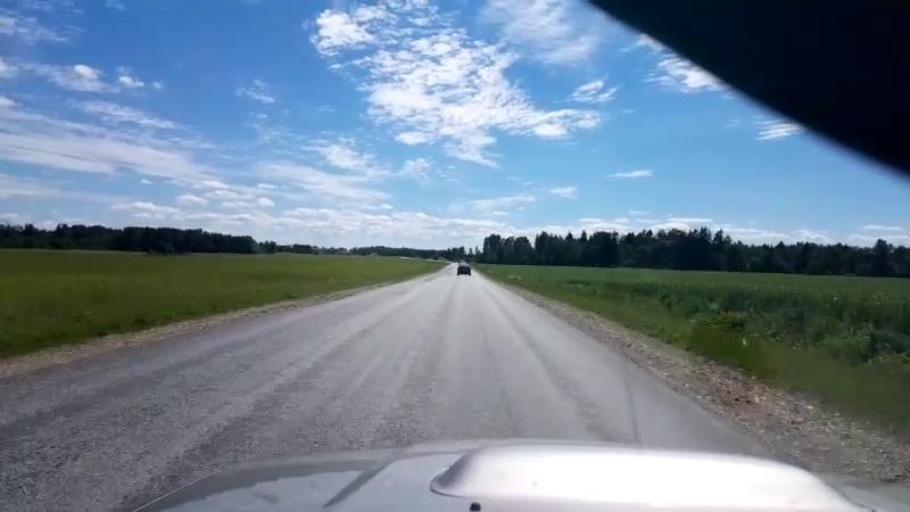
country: EE
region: Jogevamaa
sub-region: Jogeva linn
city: Jogeva
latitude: 58.8303
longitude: 26.2873
